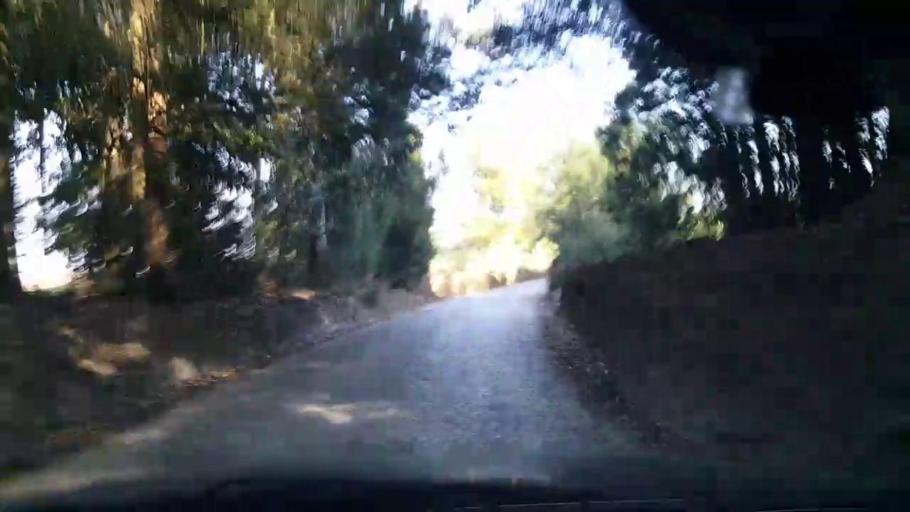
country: PT
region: Porto
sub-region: Vila do Conde
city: Arvore
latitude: 41.3499
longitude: -8.6971
